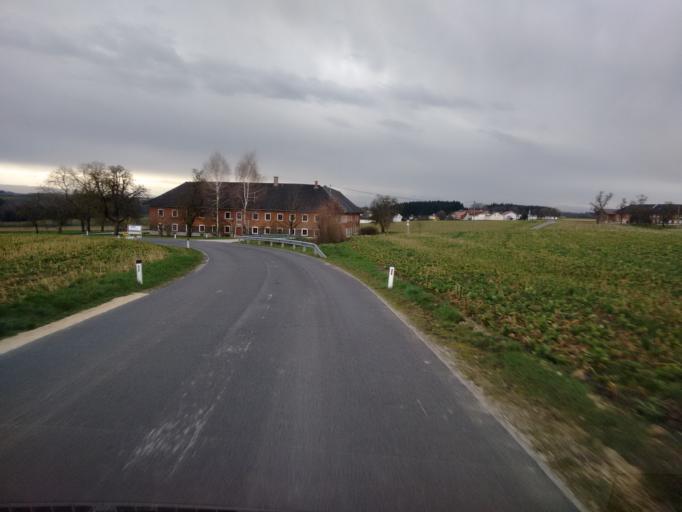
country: AT
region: Upper Austria
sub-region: Politischer Bezirk Linz-Land
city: Ansfelden
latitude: 48.1334
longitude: 14.2571
